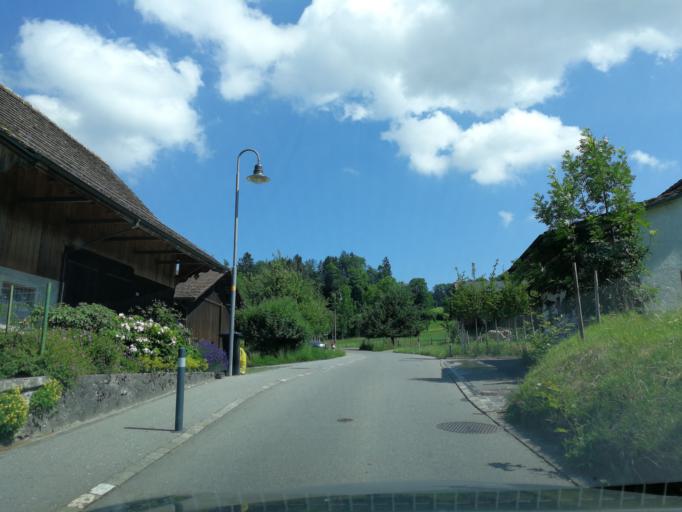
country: CH
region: Zurich
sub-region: Bezirk Meilen
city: Meilen
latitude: 47.2792
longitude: 8.6439
